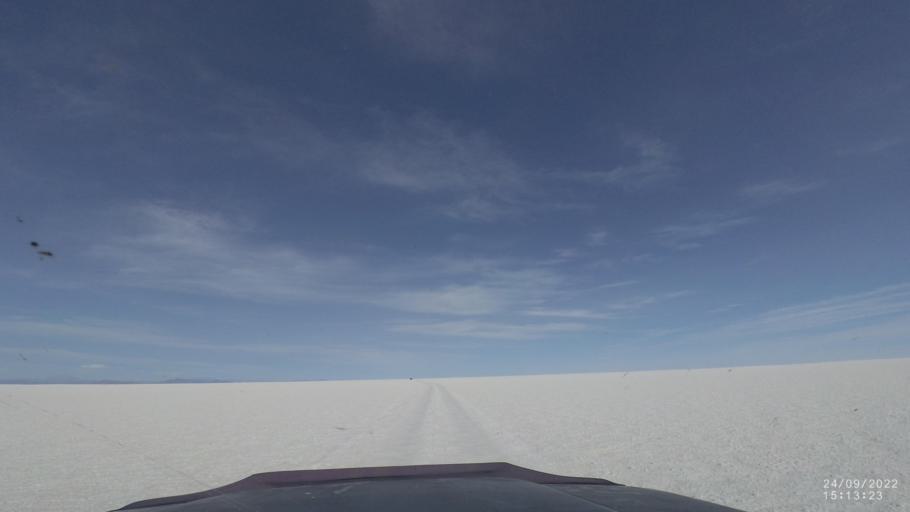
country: BO
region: Potosi
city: Colchani
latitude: -19.9556
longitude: -67.4652
